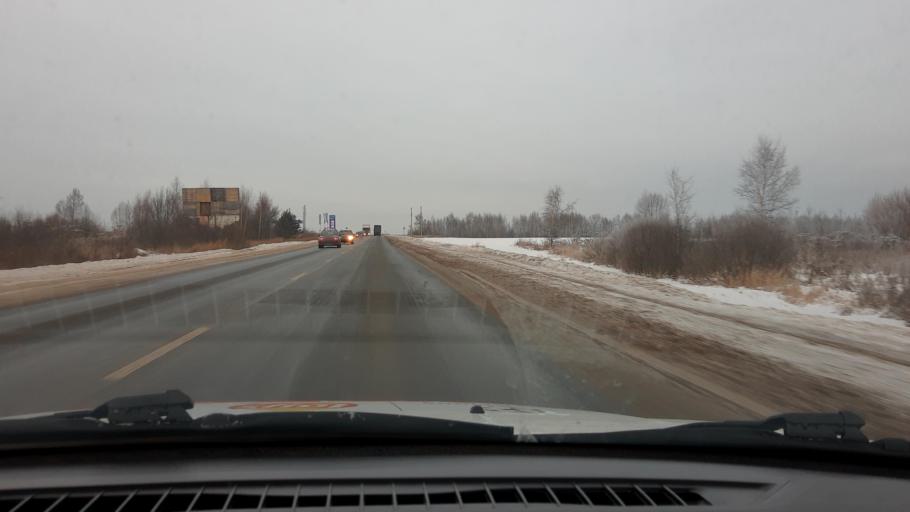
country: RU
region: Nizjnij Novgorod
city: Sitniki
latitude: 56.4894
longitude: 44.0217
